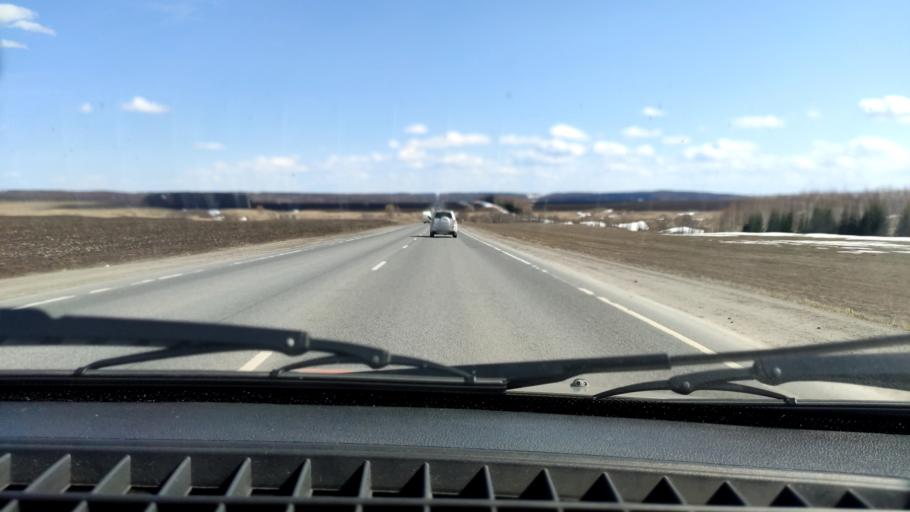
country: RU
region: Bashkortostan
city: Iglino
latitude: 54.7542
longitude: 56.3521
